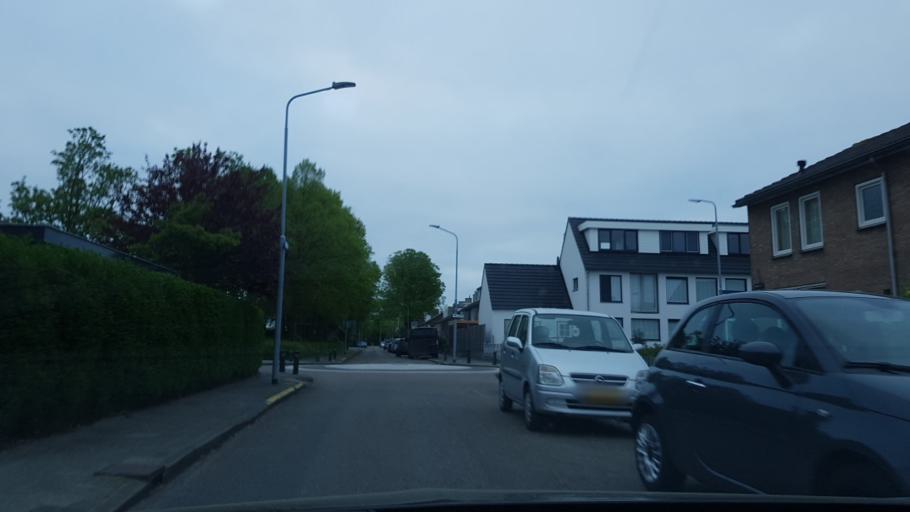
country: NL
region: South Holland
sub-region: Gemeente Kaag en Braassem
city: Oude Wetering
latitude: 52.2611
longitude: 4.6372
